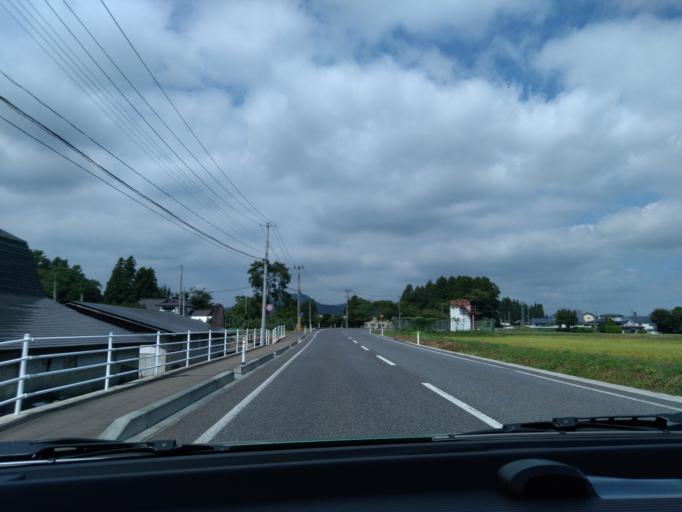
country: JP
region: Iwate
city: Hanamaki
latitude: 39.3834
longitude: 141.0554
